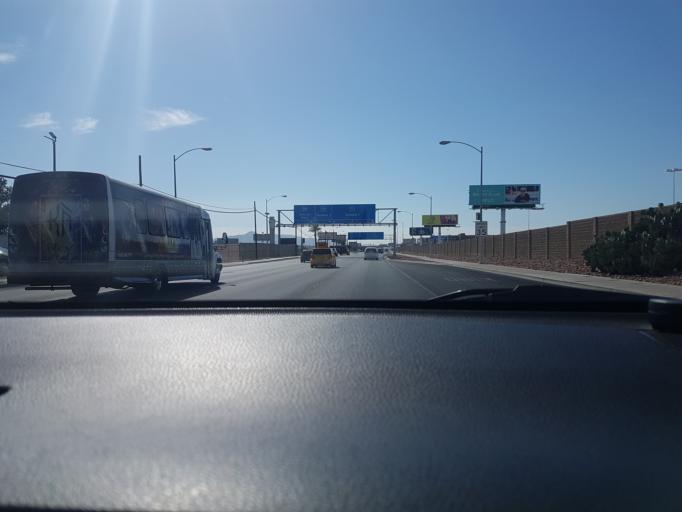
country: US
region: Nevada
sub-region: Clark County
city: Paradise
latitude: 36.0976
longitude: -115.1489
